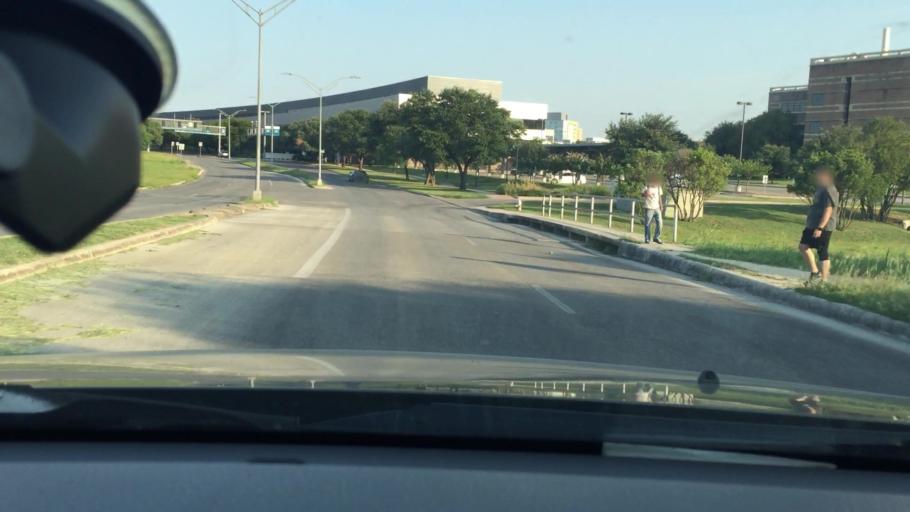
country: US
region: Texas
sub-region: Bexar County
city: Leon Valley
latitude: 29.5161
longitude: -98.5851
